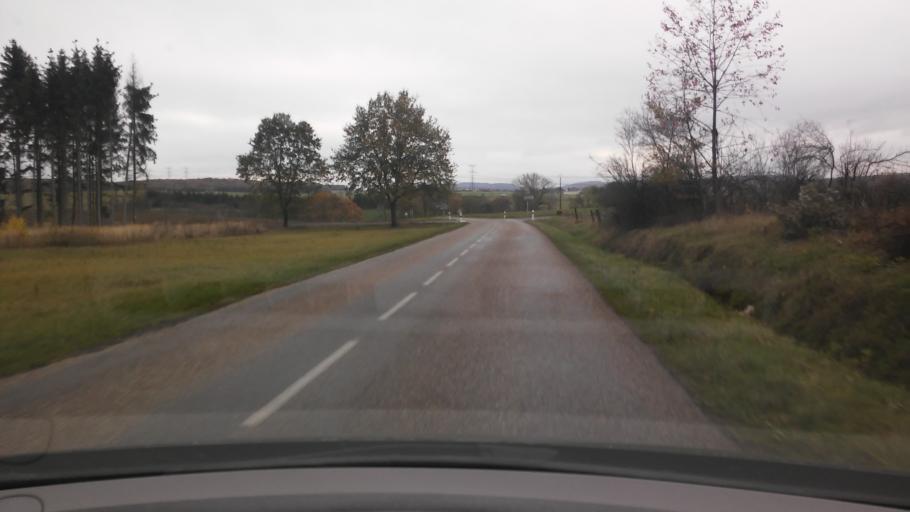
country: FR
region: Lorraine
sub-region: Departement de la Moselle
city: Metzervisse
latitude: 49.2920
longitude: 6.2764
